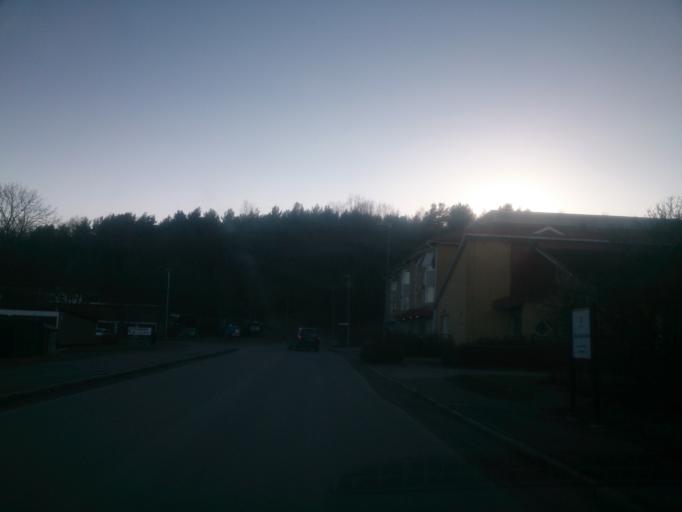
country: SE
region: OEstergoetland
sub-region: Norrkopings Kommun
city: Norrkoping
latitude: 58.5631
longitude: 16.2127
